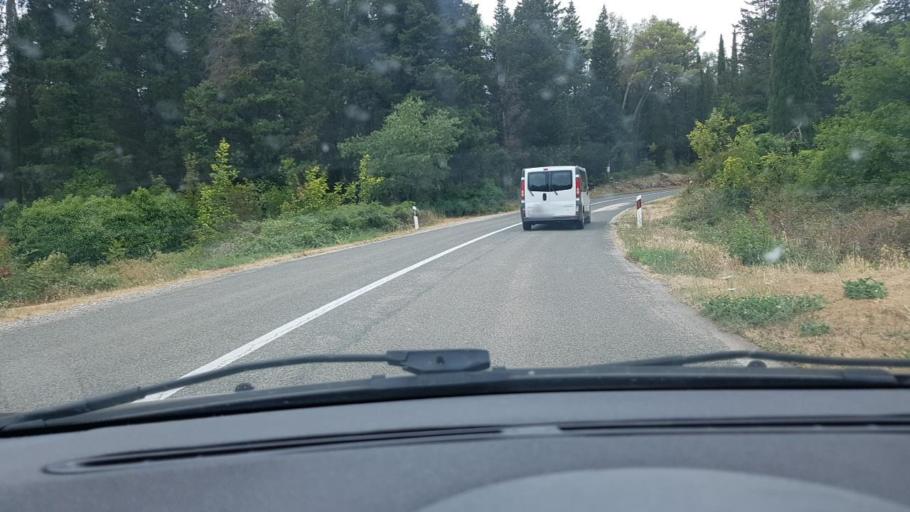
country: HR
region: Dubrovacko-Neretvanska
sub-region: Grad Korcula
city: Zrnovo
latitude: 42.9476
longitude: 17.0351
